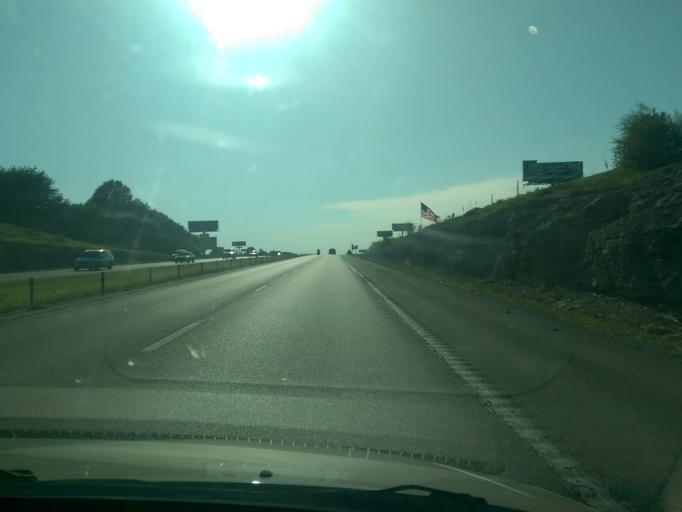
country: US
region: Missouri
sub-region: Jackson County
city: Grain Valley
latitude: 39.0240
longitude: -94.2185
